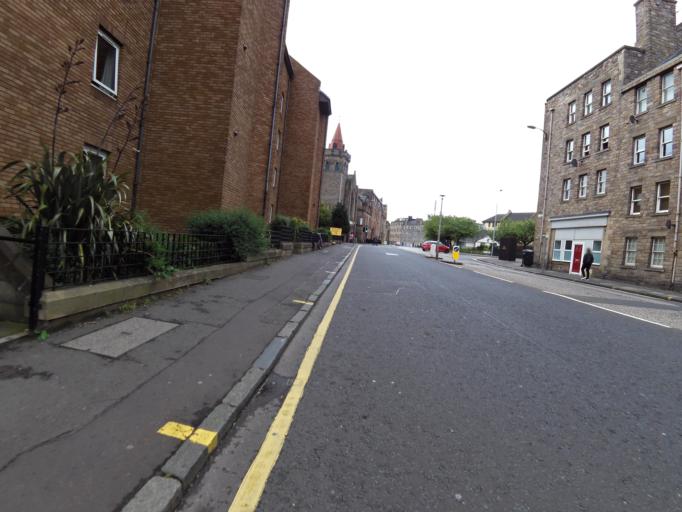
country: GB
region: Scotland
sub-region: Edinburgh
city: Edinburgh
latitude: 55.9463
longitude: -3.1815
